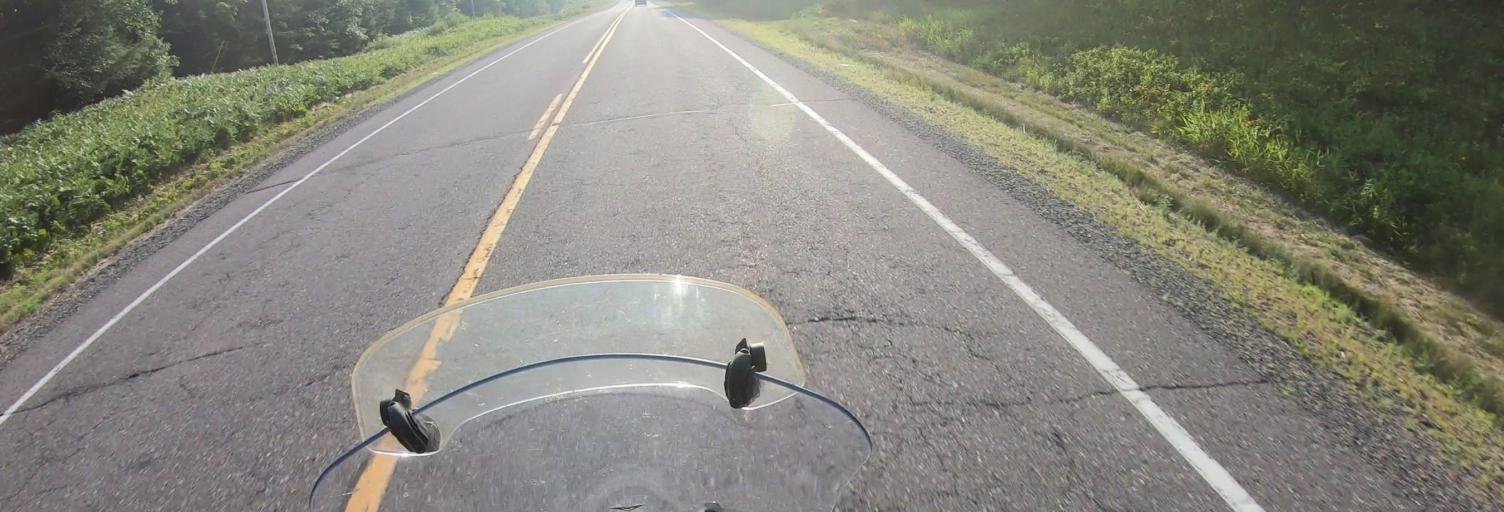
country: US
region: Wisconsin
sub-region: Sawyer County
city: Little Round Lake
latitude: 46.0712
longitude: -91.0983
